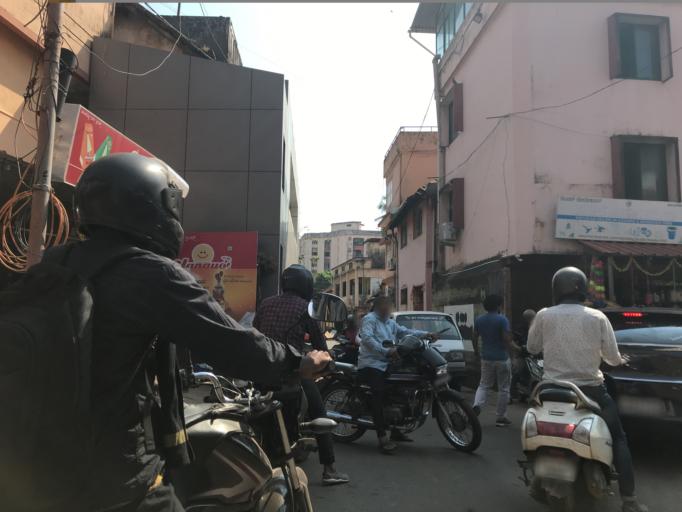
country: IN
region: Karnataka
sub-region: Dakshina Kannada
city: Mangalore
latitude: 12.8696
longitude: 74.8343
